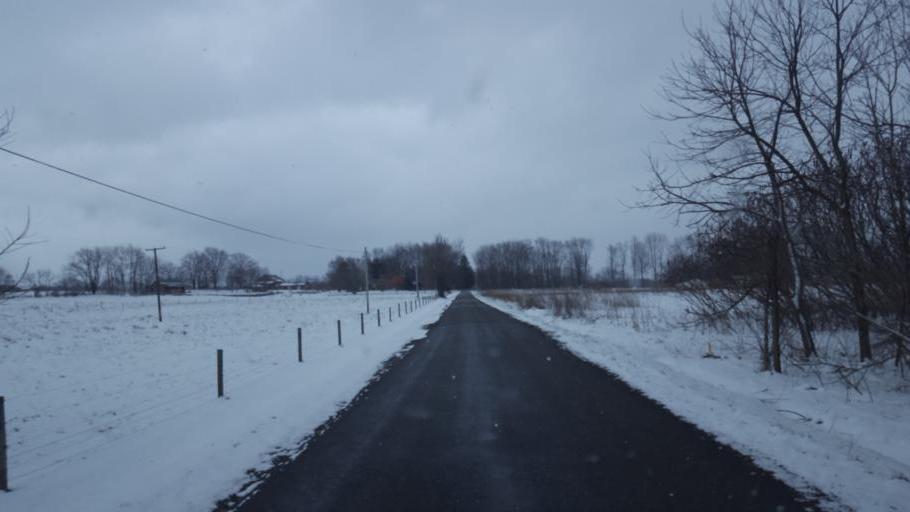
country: US
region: Pennsylvania
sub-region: Mercer County
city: Stoneboro
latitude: 41.3981
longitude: -80.0840
